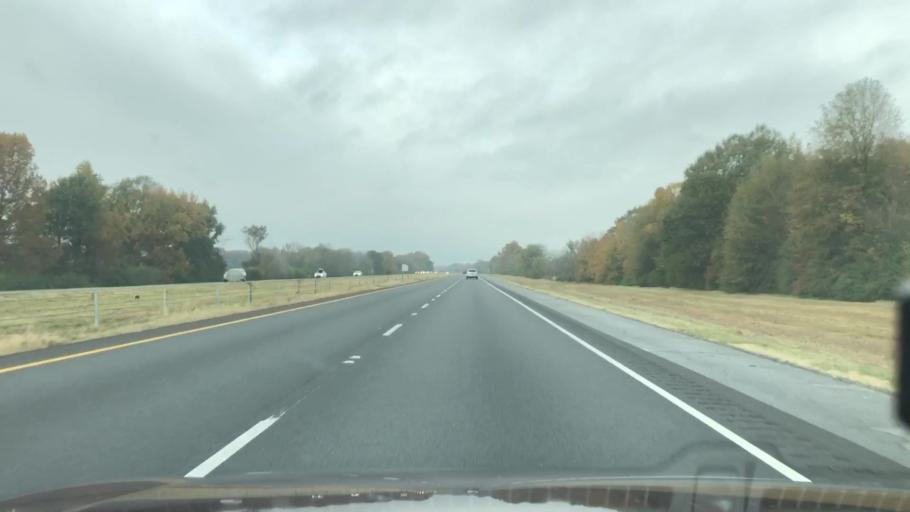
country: US
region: Louisiana
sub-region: Richland Parish
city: Rayville
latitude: 32.4631
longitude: -91.7888
